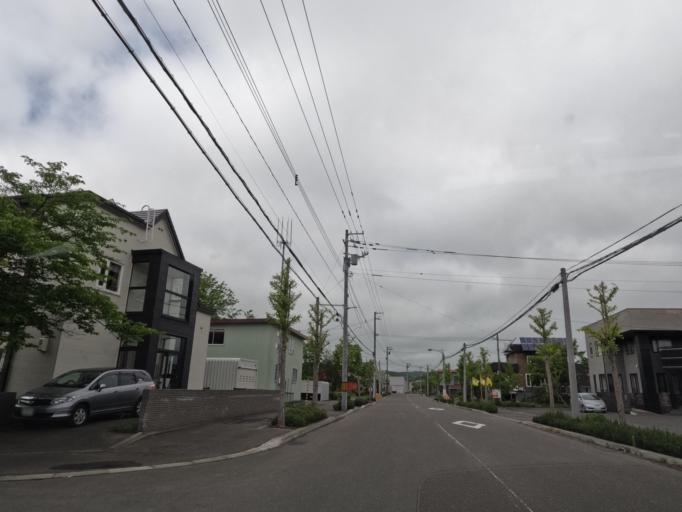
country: JP
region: Hokkaido
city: Tobetsu
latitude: 43.2311
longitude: 141.5162
